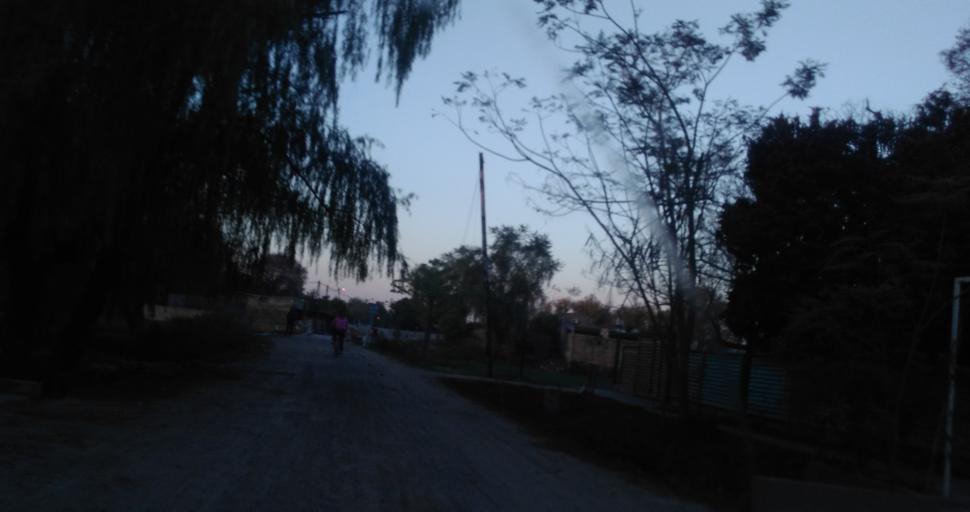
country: AR
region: Chaco
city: Resistencia
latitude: -27.4317
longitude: -58.9898
